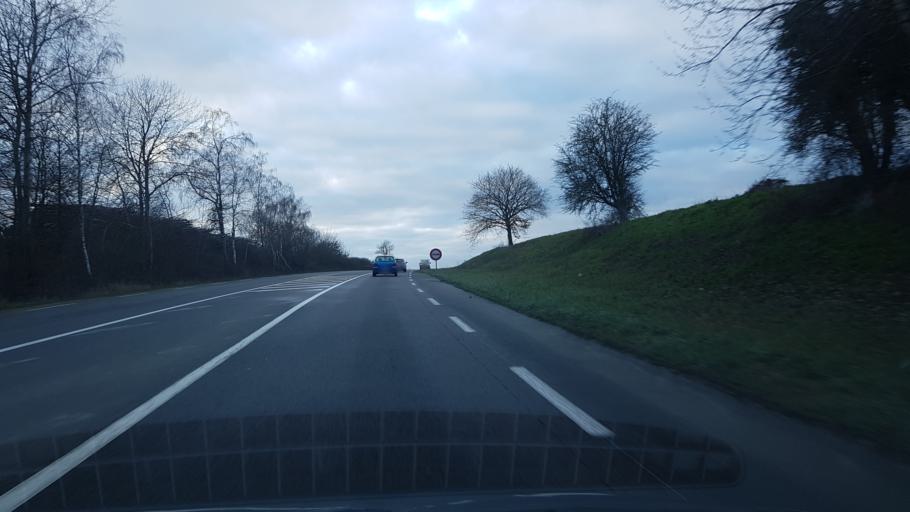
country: FR
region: Champagne-Ardenne
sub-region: Departement de la Marne
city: Esternay
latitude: 48.7198
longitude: 3.5541
